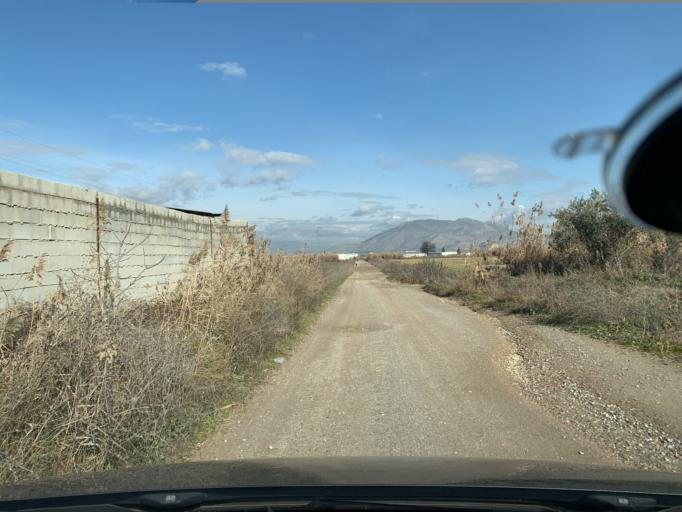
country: ES
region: Andalusia
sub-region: Provincia de Granada
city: Chauchina
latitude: 37.1821
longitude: -3.7503
